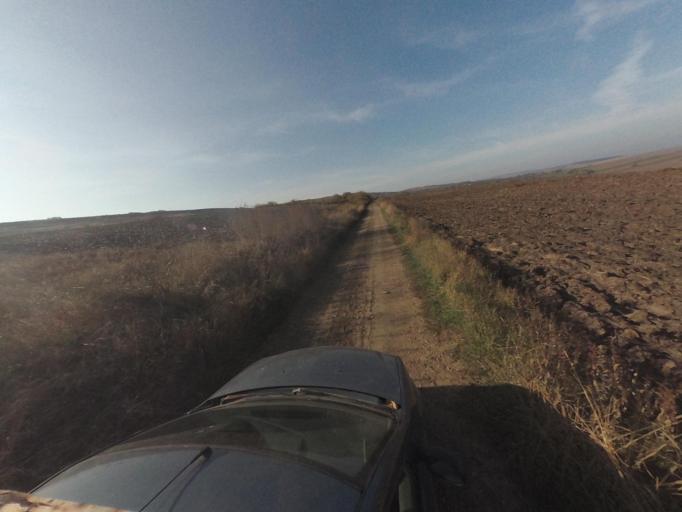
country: RO
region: Neamt
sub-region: Comuna Pancesti
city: Pancesti
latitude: 46.8769
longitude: 27.1932
